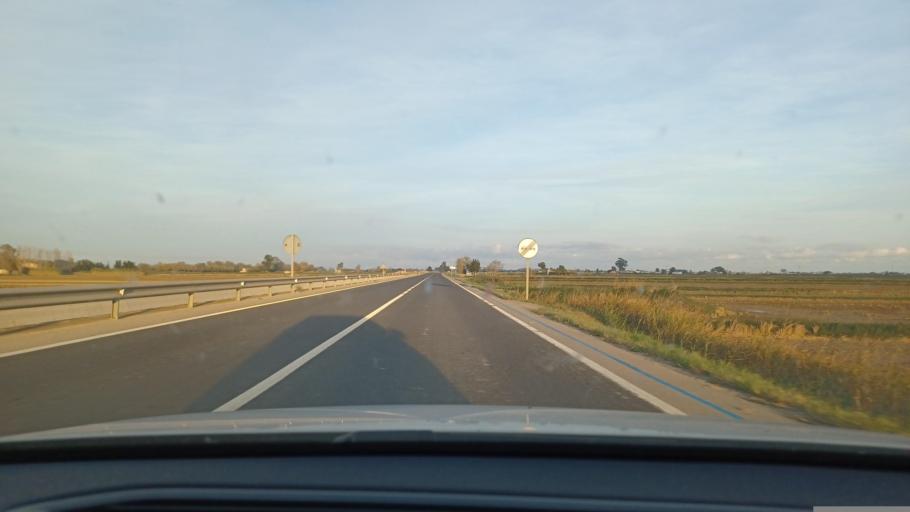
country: ES
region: Catalonia
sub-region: Provincia de Tarragona
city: Amposta
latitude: 40.7080
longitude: 0.6419
